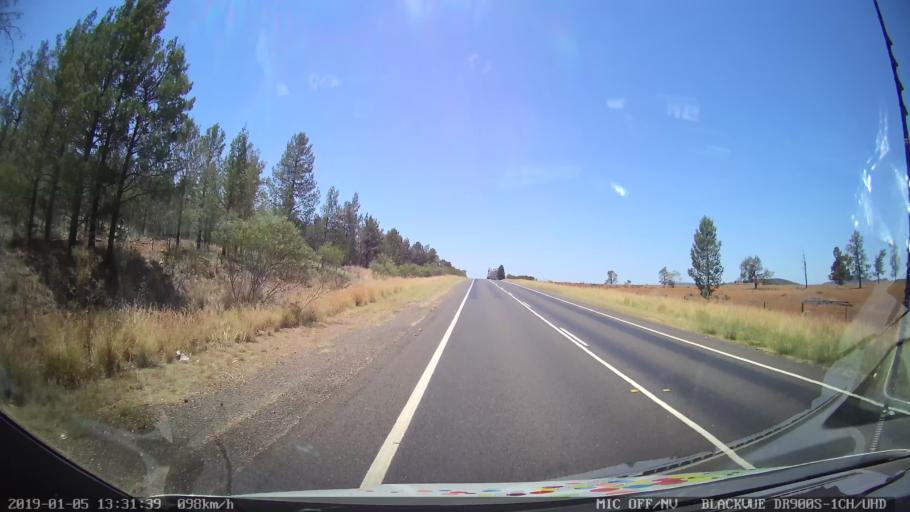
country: AU
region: New South Wales
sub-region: Gunnedah
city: Gunnedah
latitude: -31.0094
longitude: 150.0876
